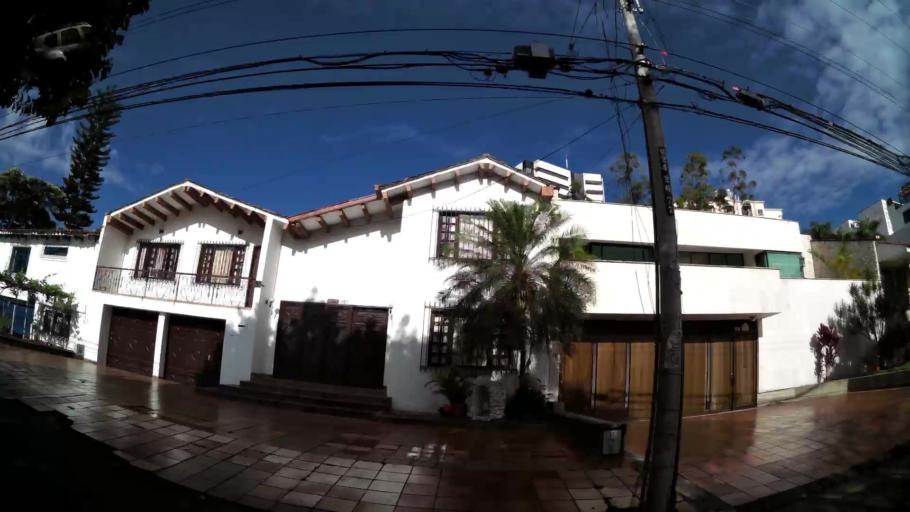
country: CO
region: Valle del Cauca
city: Cali
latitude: 3.4370
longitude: -76.5476
